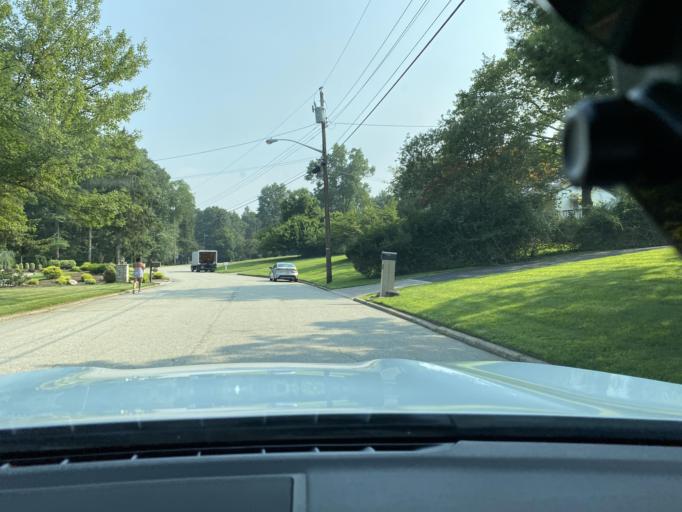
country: US
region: New York
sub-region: Rockland County
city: Airmont
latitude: 41.0829
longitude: -74.1146
